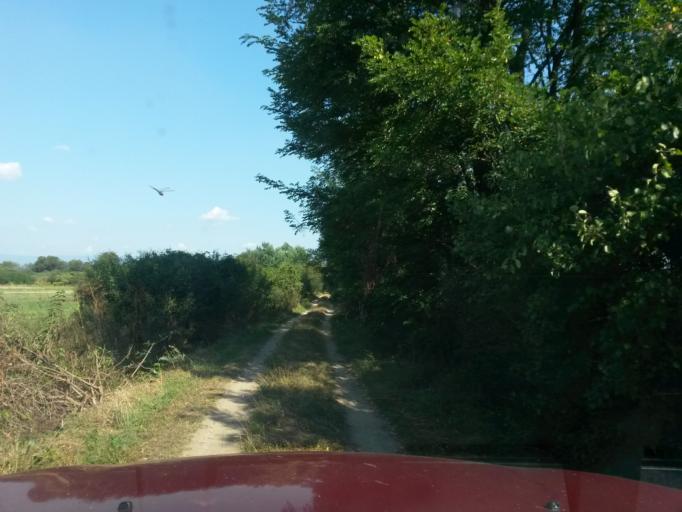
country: HU
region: Borsod-Abauj-Zemplen
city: Gonc
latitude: 48.5372
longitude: 21.1563
